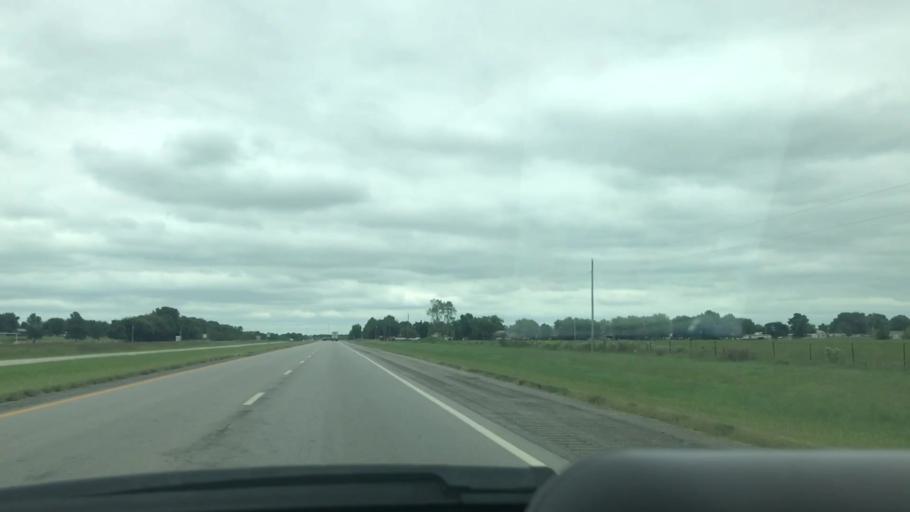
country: US
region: Oklahoma
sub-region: Mayes County
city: Pryor
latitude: 36.3325
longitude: -95.3094
